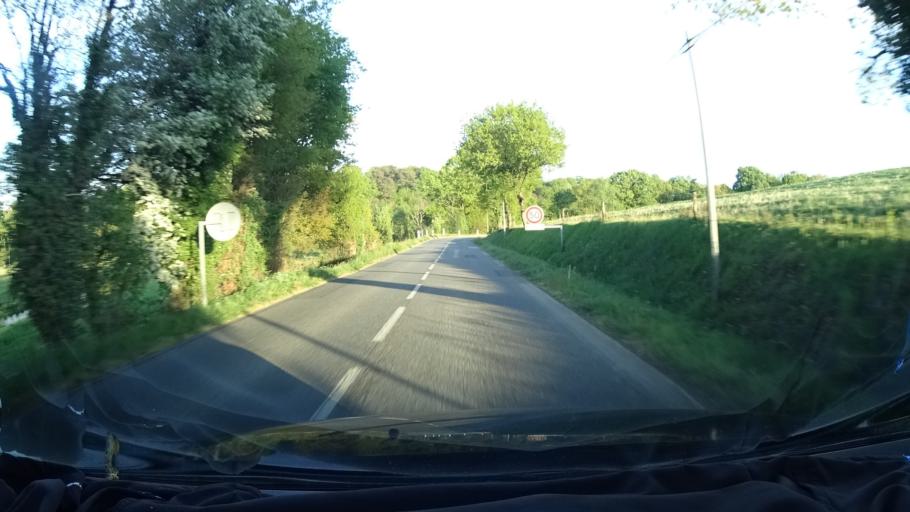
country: FR
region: Brittany
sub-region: Departement du Morbihan
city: Caden
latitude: 47.5950
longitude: -2.2973
